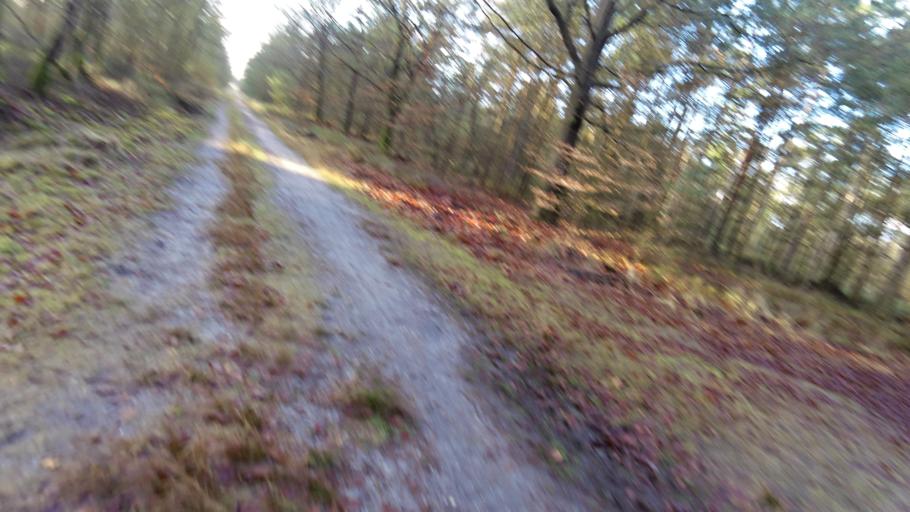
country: NL
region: Gelderland
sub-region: Gemeente Epe
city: Vaassen
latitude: 52.2930
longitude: 5.9230
